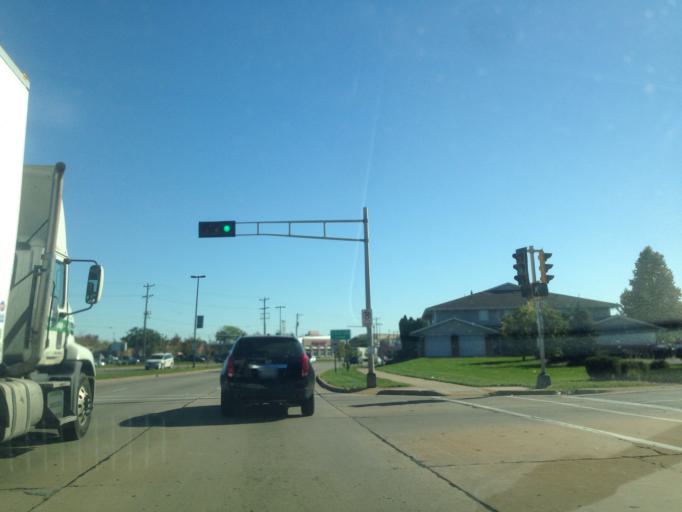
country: US
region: Wisconsin
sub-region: Milwaukee County
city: West Milwaukee
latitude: 43.0191
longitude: -87.9688
